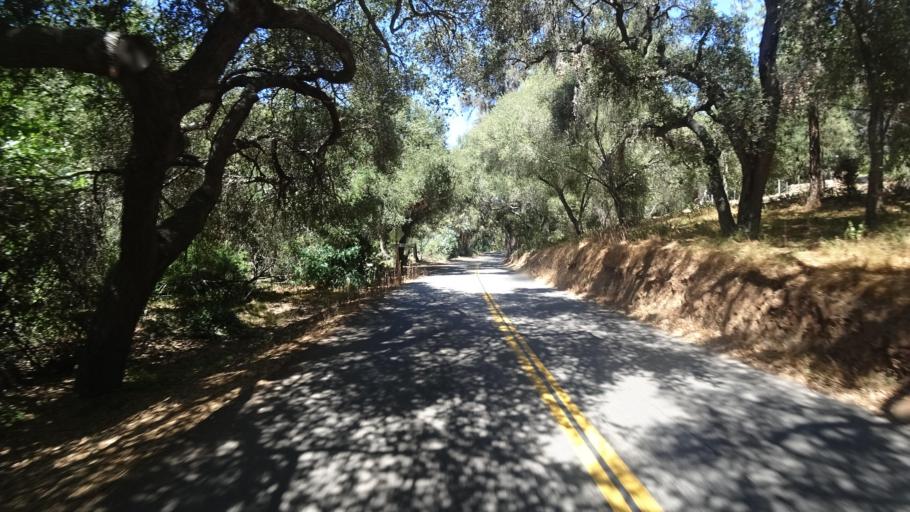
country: US
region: California
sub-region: San Diego County
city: Hidden Meadows
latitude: 33.3191
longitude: -117.1019
